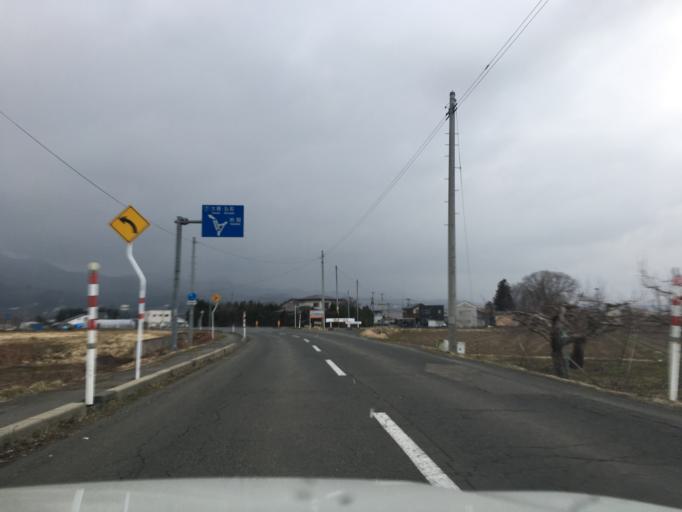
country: JP
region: Aomori
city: Hirosaki
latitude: 40.5601
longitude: 140.5482
